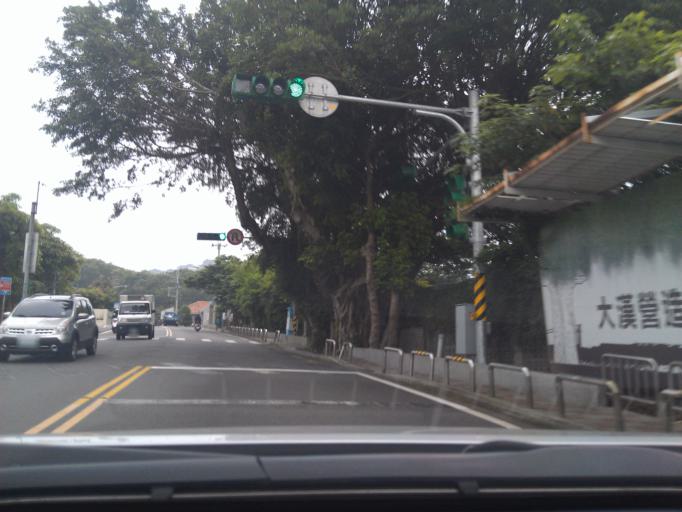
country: TW
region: Taipei
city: Taipei
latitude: 25.1193
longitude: 121.5528
